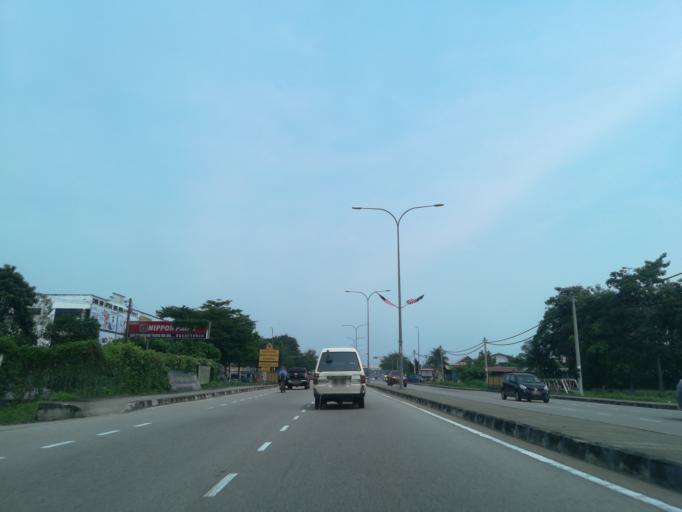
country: MY
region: Kedah
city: Kulim
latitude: 5.3875
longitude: 100.5681
